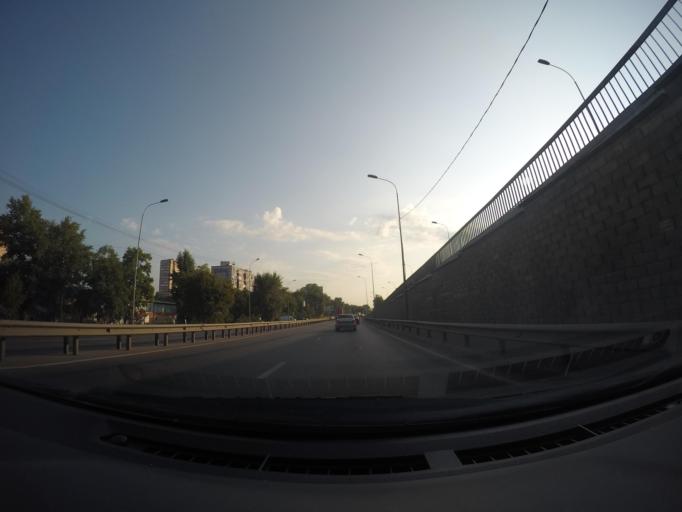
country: RU
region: Moskovskaya
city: Lyubertsy
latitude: 55.6671
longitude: 37.8832
